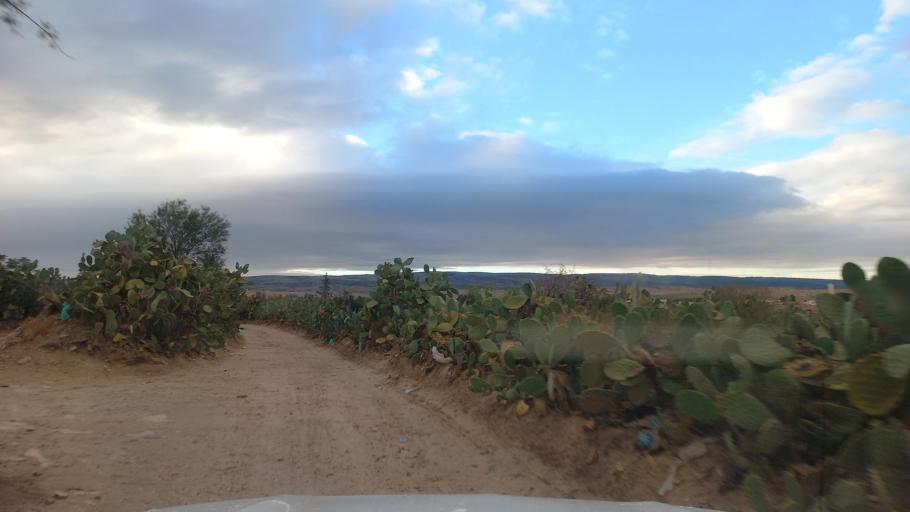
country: TN
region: Al Qasrayn
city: Kasserine
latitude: 35.2593
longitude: 8.9356
